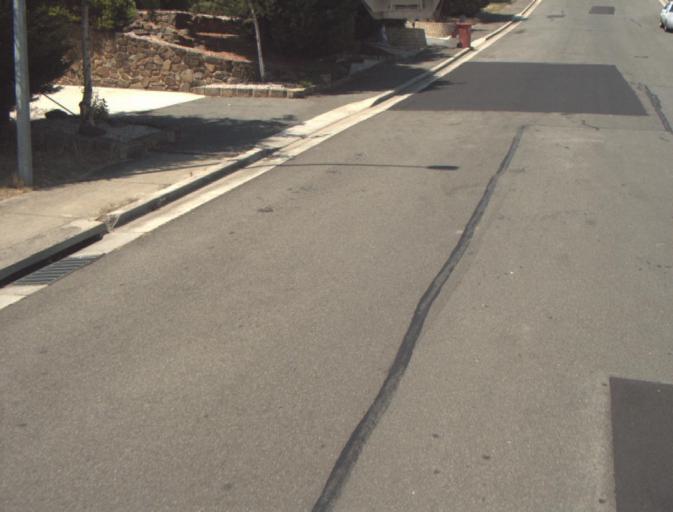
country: AU
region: Tasmania
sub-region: Launceston
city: Newstead
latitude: -41.4835
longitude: 147.1785
